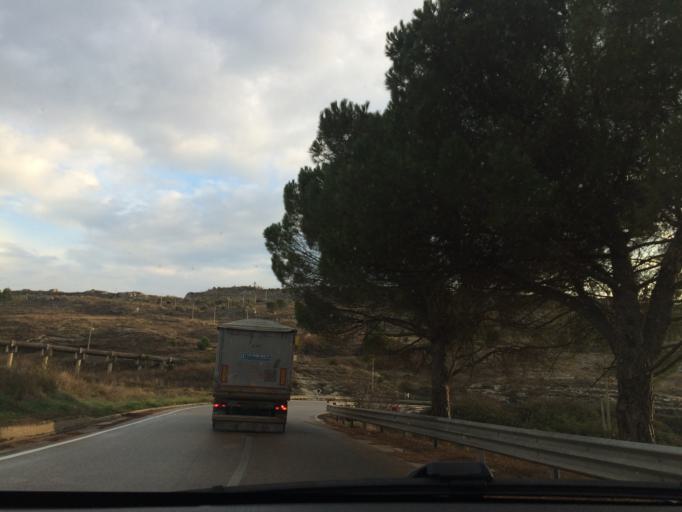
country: IT
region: Basilicate
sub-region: Provincia di Matera
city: Matera
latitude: 40.6777
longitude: 16.6424
